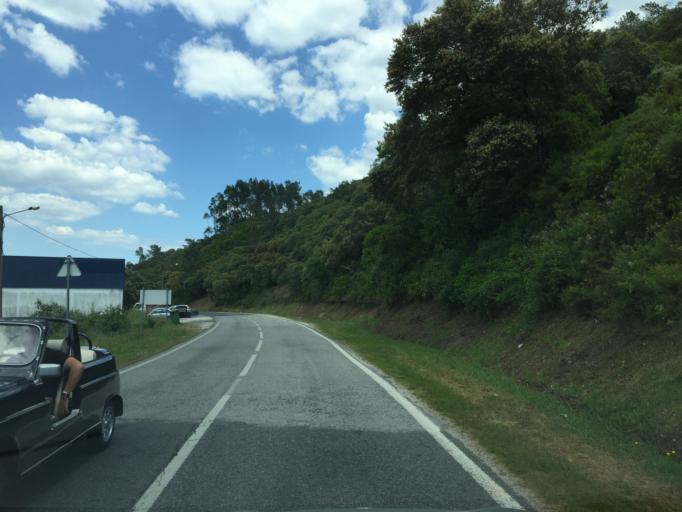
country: PT
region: Santarem
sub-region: Ourem
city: Fatima
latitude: 39.6396
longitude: -8.6272
